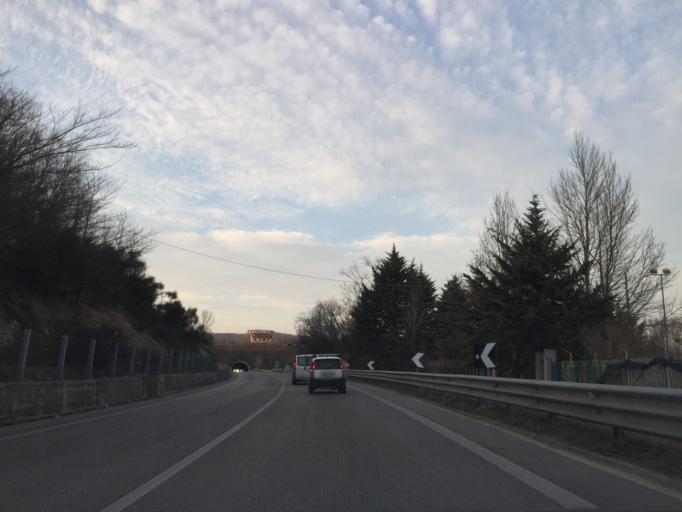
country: IT
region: Molise
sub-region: Provincia di Campobasso
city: Vinchiaturo
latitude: 41.5245
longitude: 14.6141
